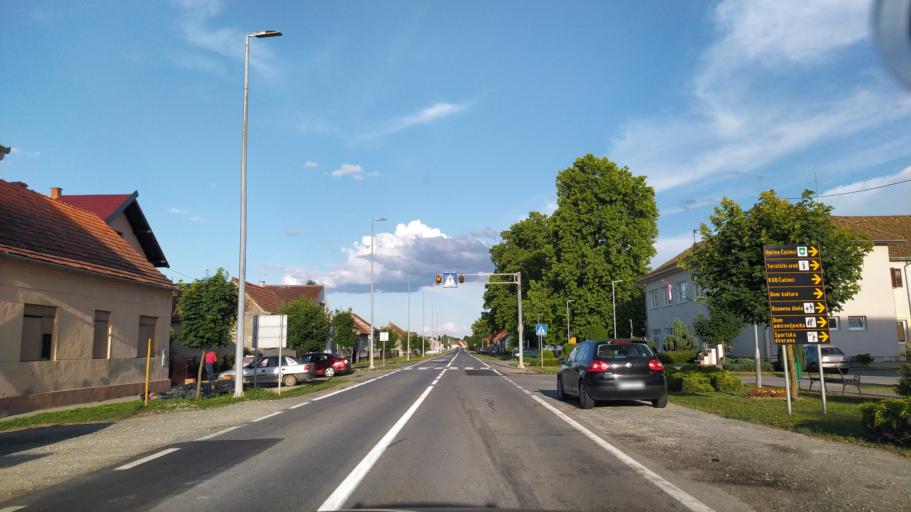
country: HR
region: Virovitick-Podravska
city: Cacinci
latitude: 45.6003
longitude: 17.8737
